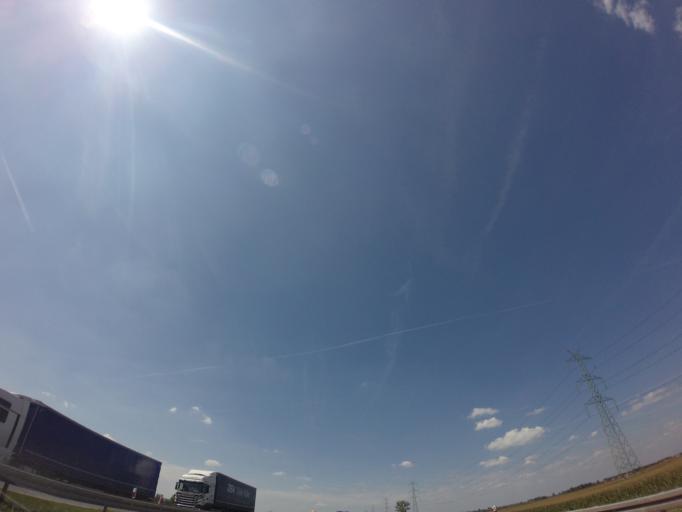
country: PL
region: Lower Silesian Voivodeship
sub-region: Powiat olawski
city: Wierzbno
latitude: 50.9308
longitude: 17.1186
